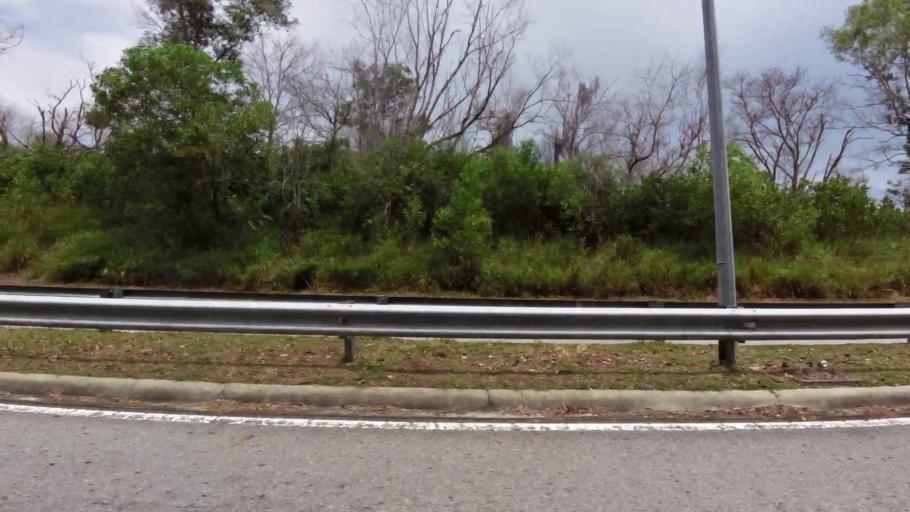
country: BN
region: Brunei and Muara
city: Bandar Seri Begawan
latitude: 4.9667
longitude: 114.8807
